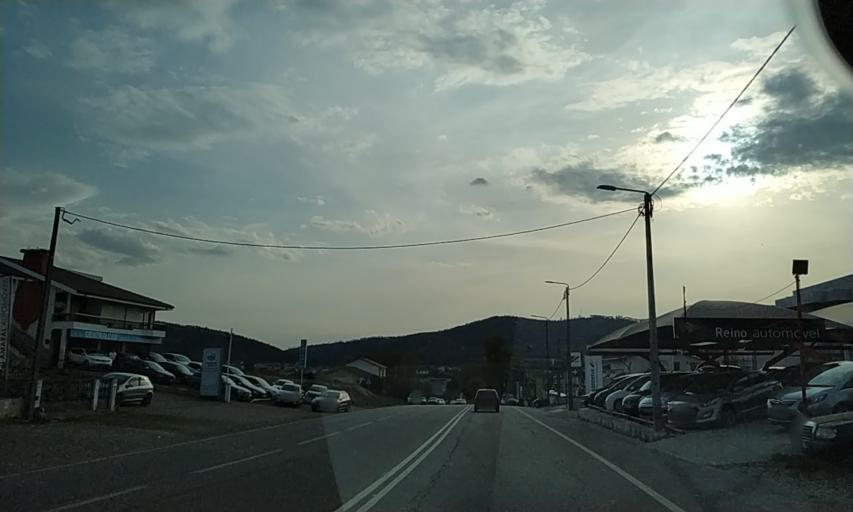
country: PT
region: Porto
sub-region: Valongo
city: Campo
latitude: 41.1855
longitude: -8.4585
